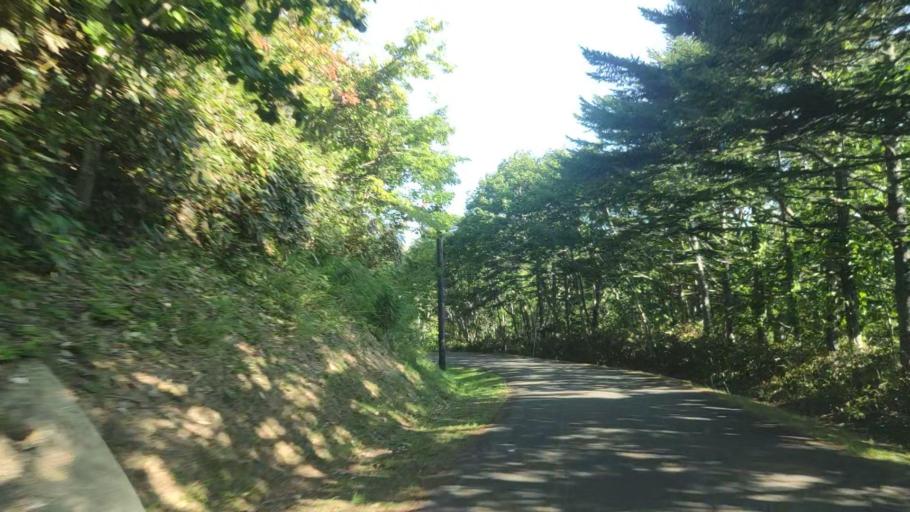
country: JP
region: Hokkaido
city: Wakkanai
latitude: 45.4137
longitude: 141.6686
